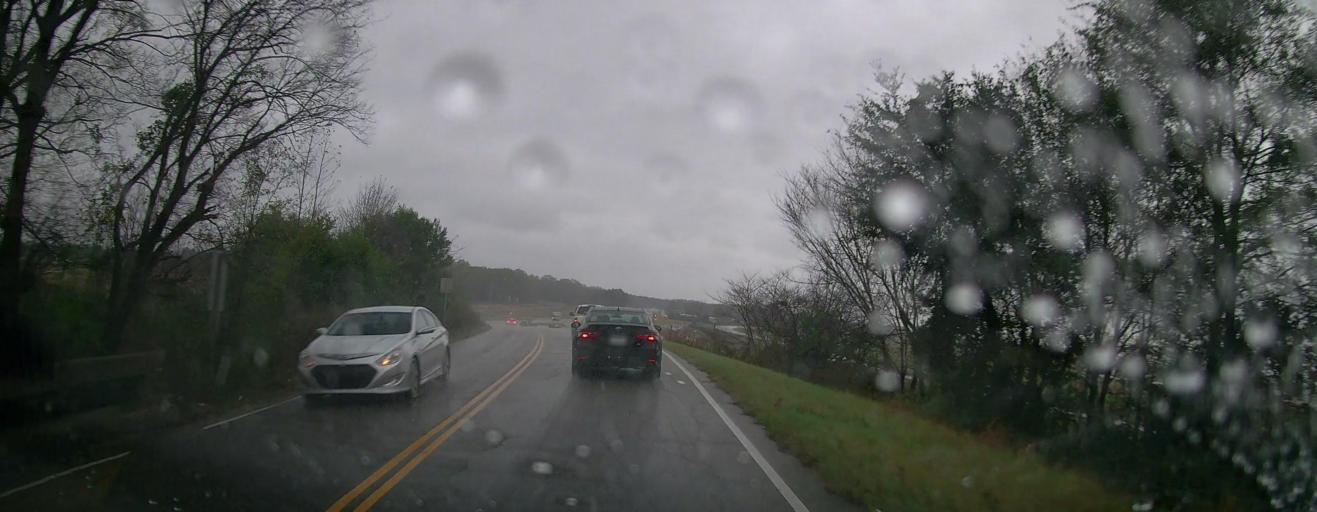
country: US
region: Alabama
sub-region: Montgomery County
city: Montgomery
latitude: 32.3697
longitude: -86.3531
